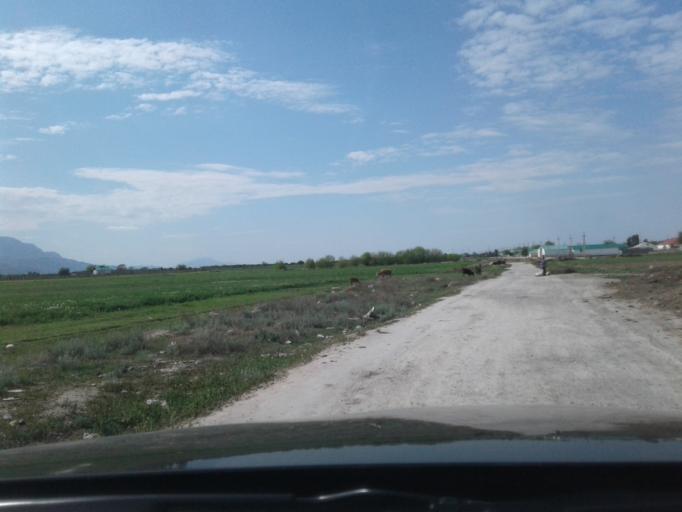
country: TM
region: Ahal
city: Ashgabat
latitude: 37.9789
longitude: 58.2912
